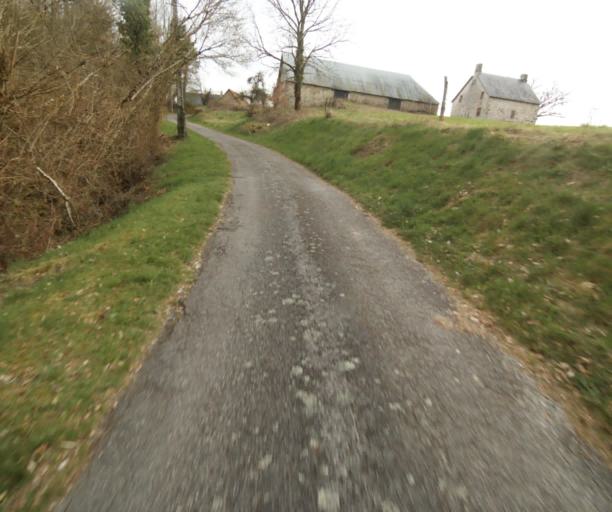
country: FR
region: Limousin
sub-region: Departement de la Correze
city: Argentat
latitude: 45.2054
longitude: 1.9906
